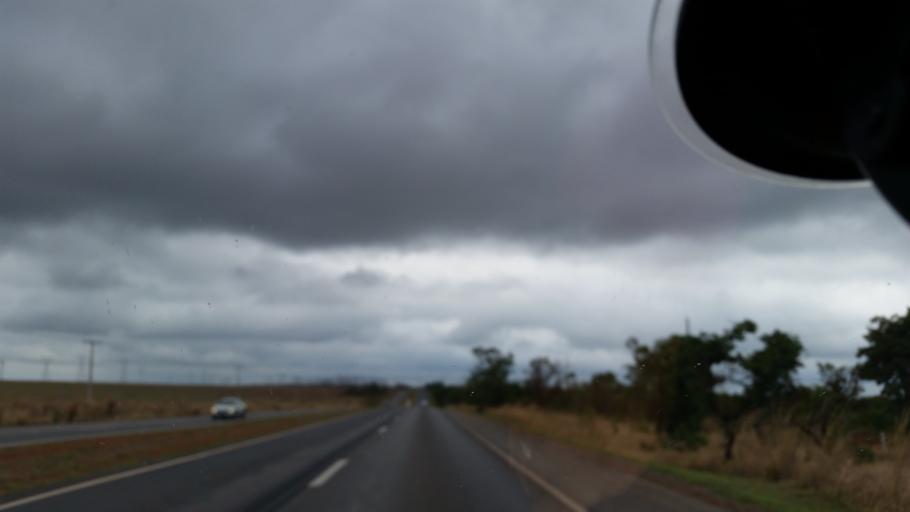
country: BR
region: Goias
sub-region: Luziania
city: Luziania
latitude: -16.3265
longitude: -47.8391
